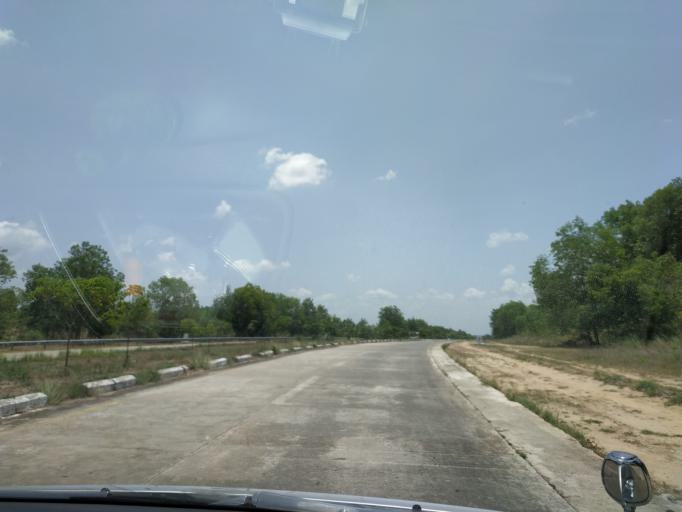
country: MM
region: Bago
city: Bago
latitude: 17.4011
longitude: 96.3292
